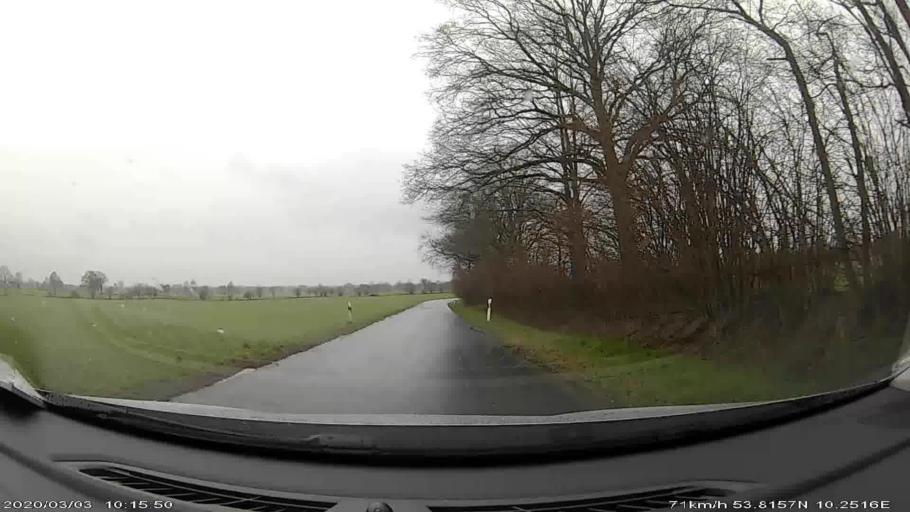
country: DE
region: Schleswig-Holstein
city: Sulfeld
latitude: 53.8138
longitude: 10.2469
